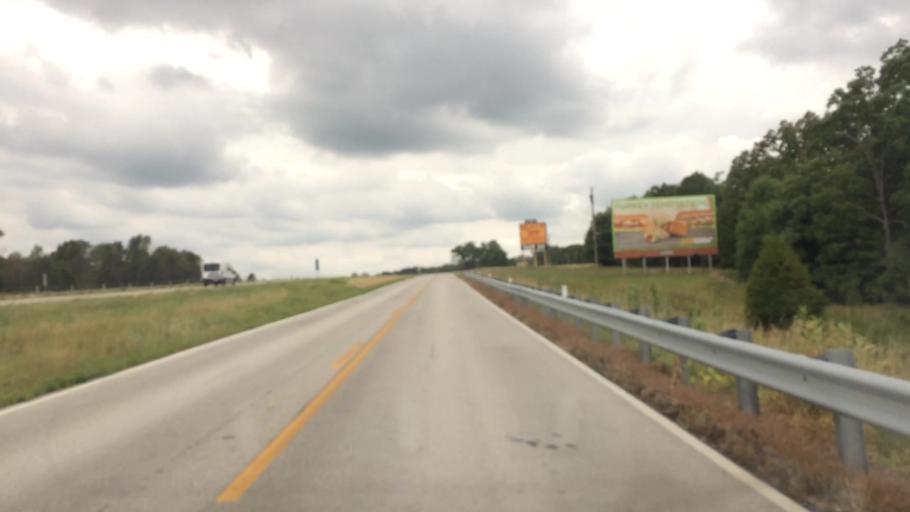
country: US
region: Missouri
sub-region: Greene County
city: Strafford
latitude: 37.2864
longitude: -93.0375
